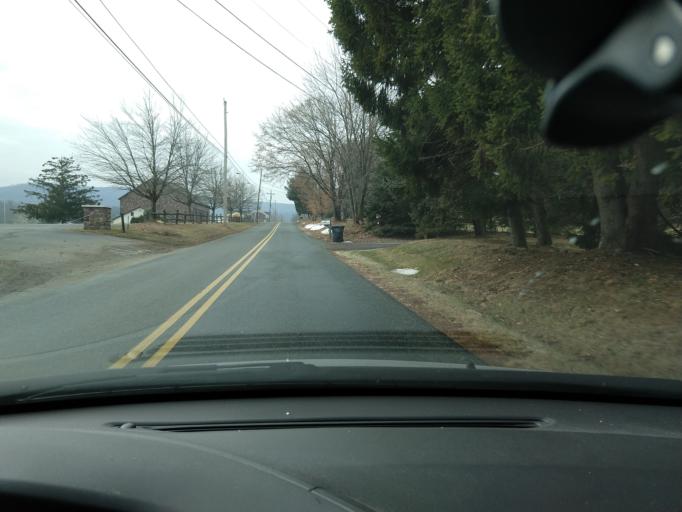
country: US
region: Pennsylvania
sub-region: Berks County
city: Amity Gardens
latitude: 40.2470
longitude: -75.7418
